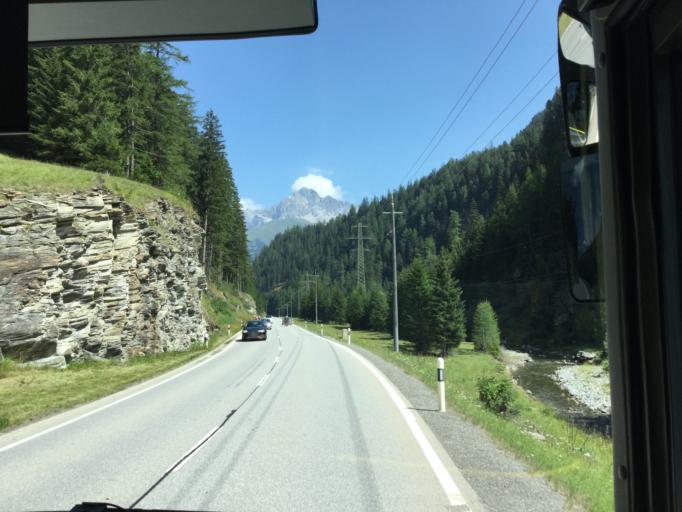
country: CH
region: Grisons
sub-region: Albula District
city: Tiefencastel
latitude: 46.5378
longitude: 9.6242
